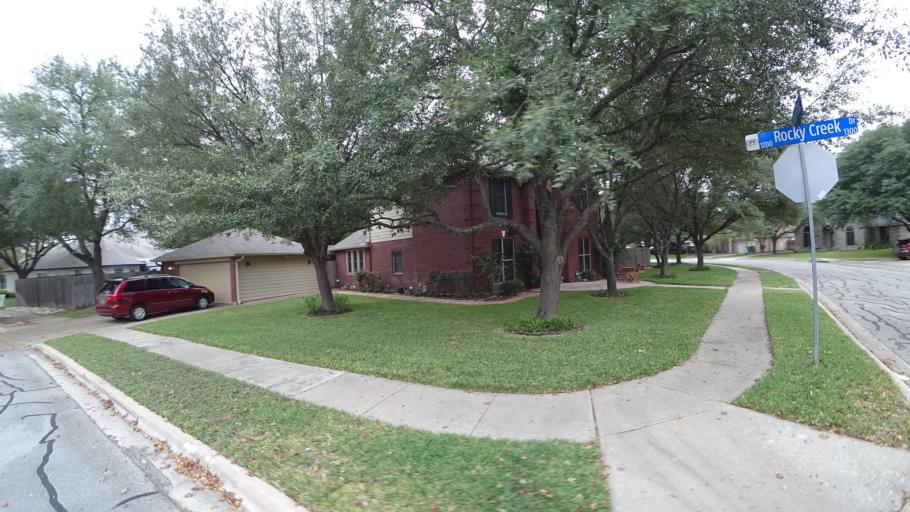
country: US
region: Texas
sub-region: Travis County
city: Pflugerville
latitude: 30.4529
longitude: -97.6157
